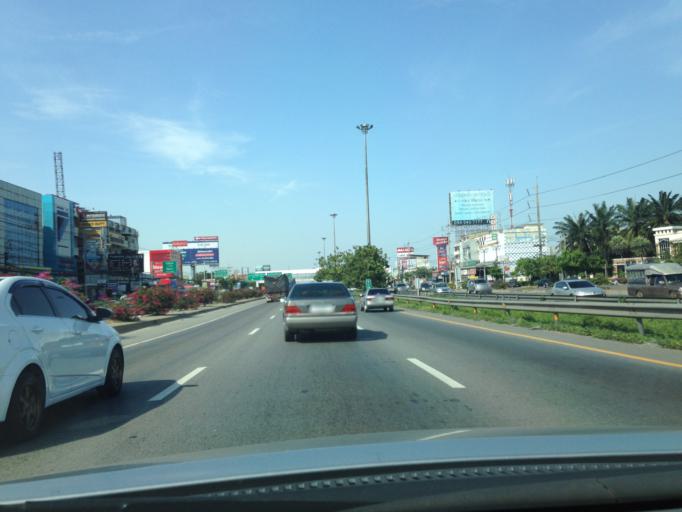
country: TH
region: Nonthaburi
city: Bang Yai
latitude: 13.8533
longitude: 100.4118
